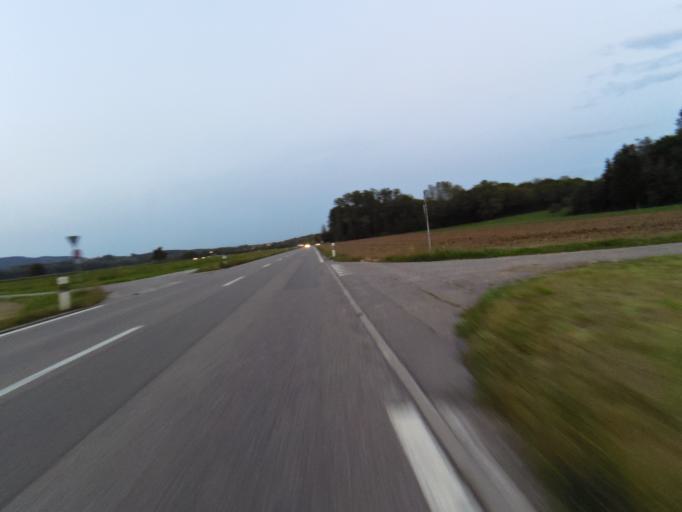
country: CH
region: Thurgau
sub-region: Frauenfeld District
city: Frauenfeld
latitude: 47.5671
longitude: 8.8746
